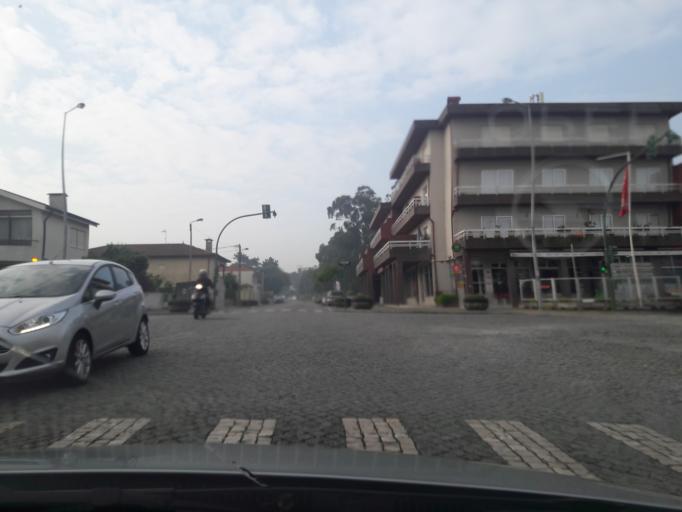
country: PT
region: Porto
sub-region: Vila do Conde
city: Arvore
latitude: 41.3327
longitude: -8.7311
